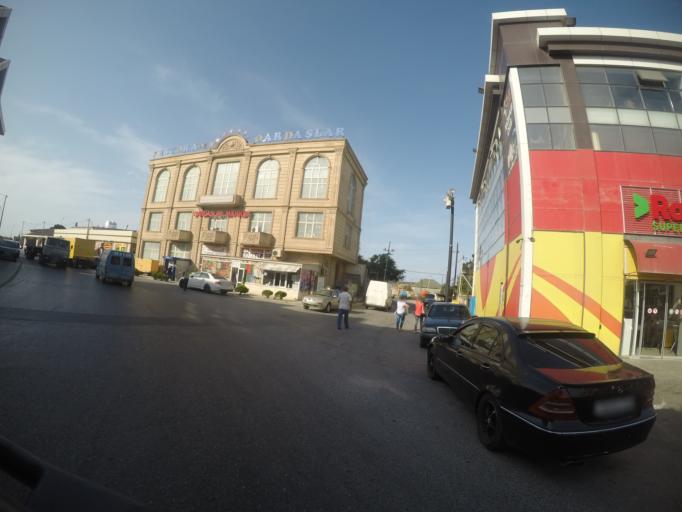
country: AZ
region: Baki
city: Binagadi
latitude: 40.4676
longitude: 49.8421
